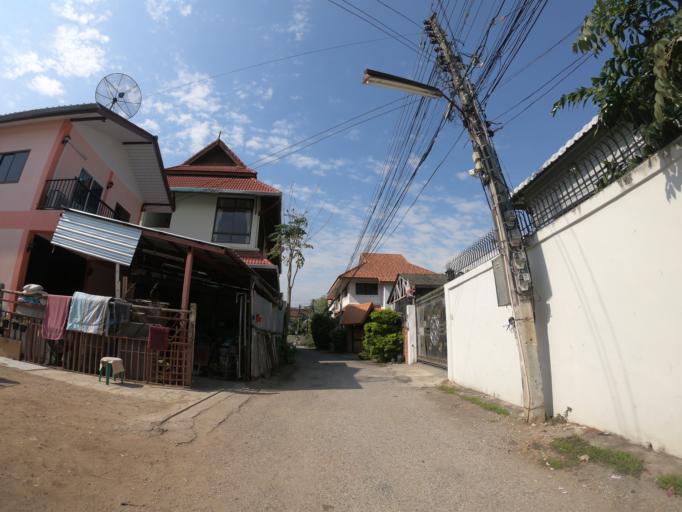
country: TH
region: Chiang Mai
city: Chiang Mai
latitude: 18.8006
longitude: 99.0110
